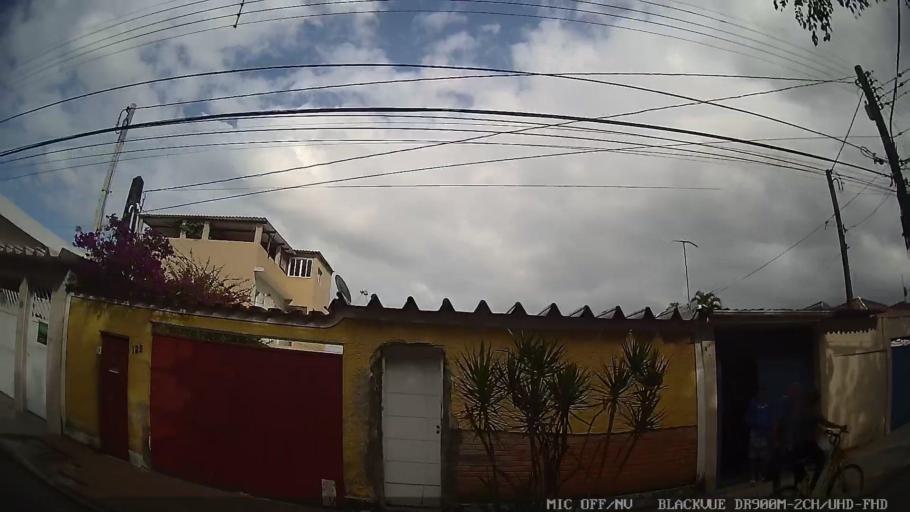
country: BR
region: Sao Paulo
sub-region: Guaruja
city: Guaruja
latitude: -23.9921
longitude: -46.2870
